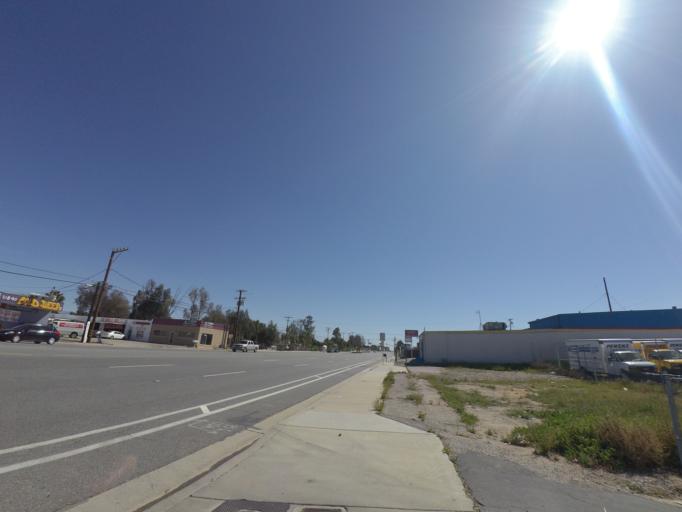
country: US
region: California
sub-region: Riverside County
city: March Air Force Base
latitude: 33.9167
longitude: -117.2817
